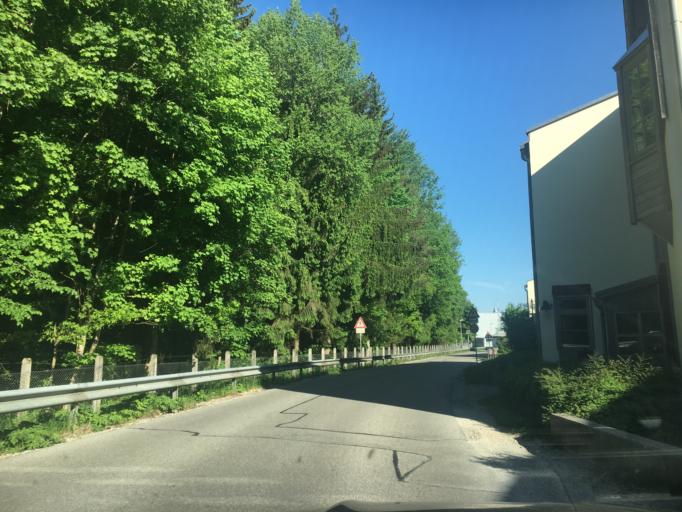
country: DE
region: Bavaria
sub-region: Upper Bavaria
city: Traunreut
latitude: 47.9585
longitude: 12.6131
